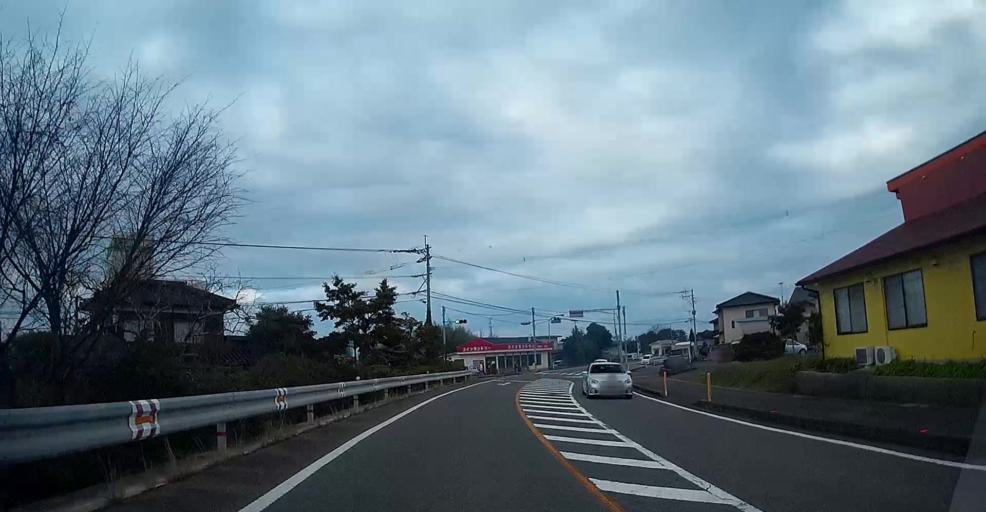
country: JP
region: Kumamoto
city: Hondo
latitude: 32.4767
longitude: 130.2609
